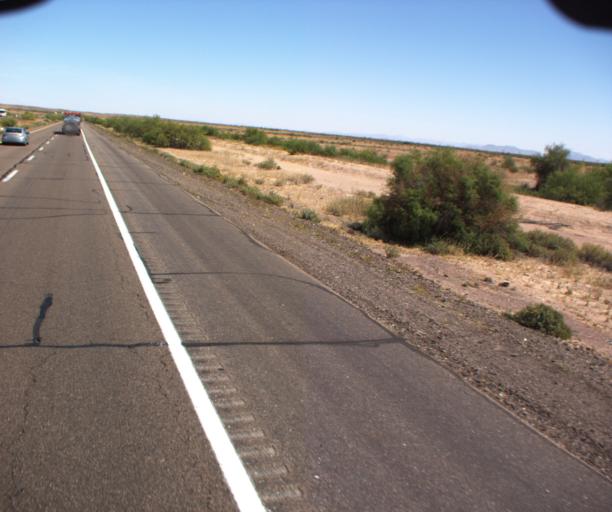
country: US
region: Arizona
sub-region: Maricopa County
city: Gila Bend
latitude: 32.8811
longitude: -113.1012
